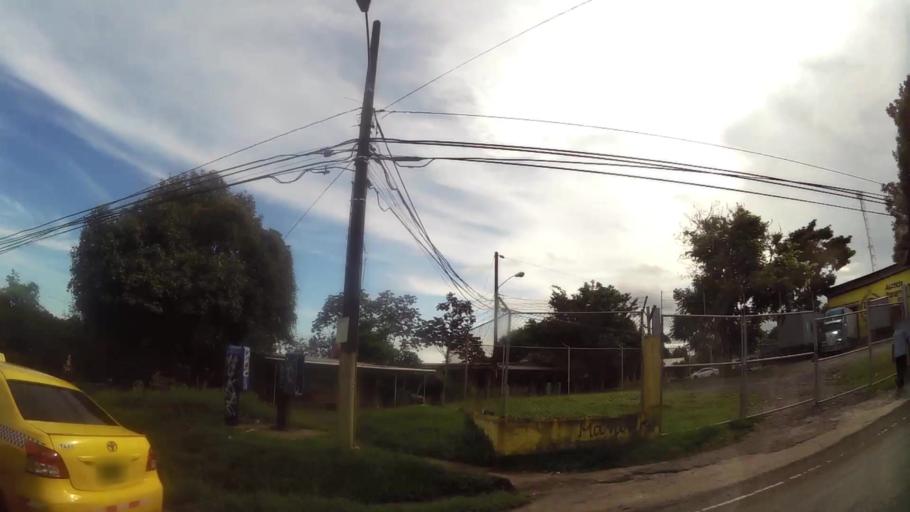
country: PA
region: Panama
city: El Coco
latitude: 8.8695
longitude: -79.8027
